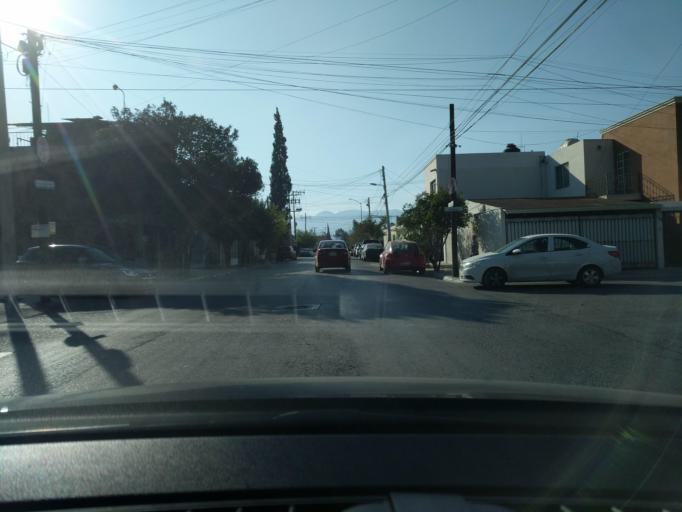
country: MX
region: Coahuila
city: Saltillo
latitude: 25.4631
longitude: -100.9860
